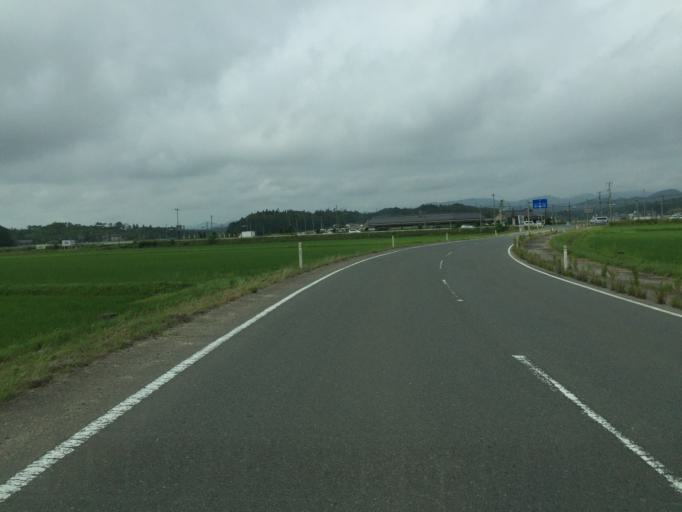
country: JP
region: Miyagi
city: Marumori
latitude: 37.7628
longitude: 140.9497
